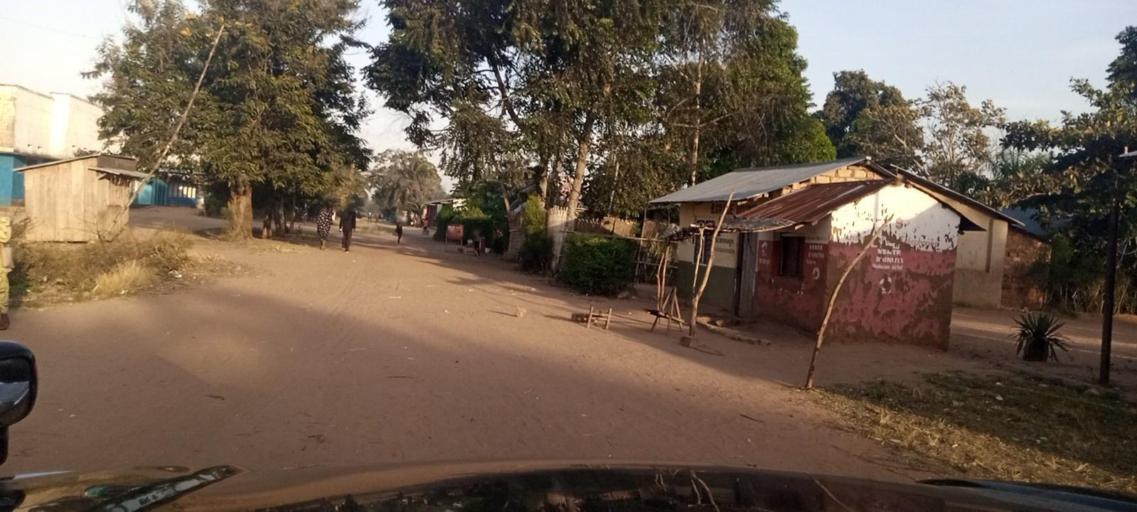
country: CD
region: Kasai-Oriental
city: Lubao
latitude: -5.3847
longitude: 25.7456
